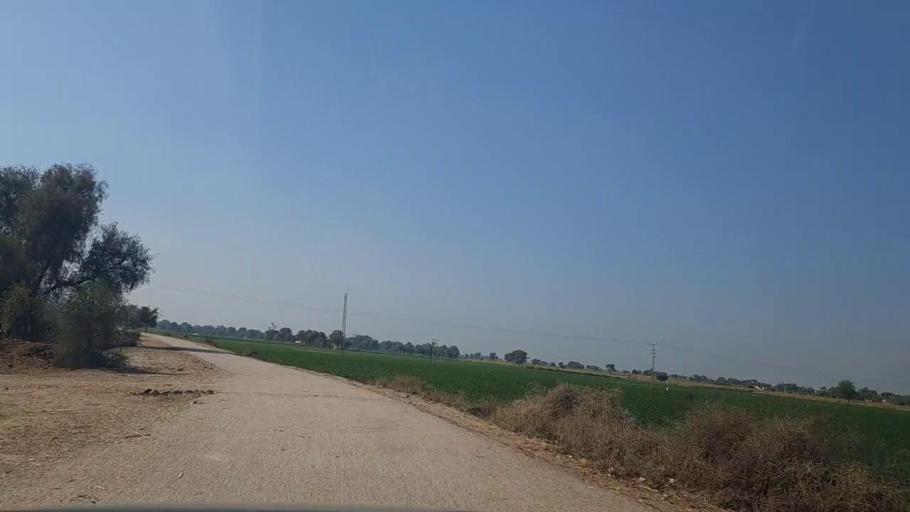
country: PK
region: Sindh
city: Daulatpur
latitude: 26.2847
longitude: 68.0466
